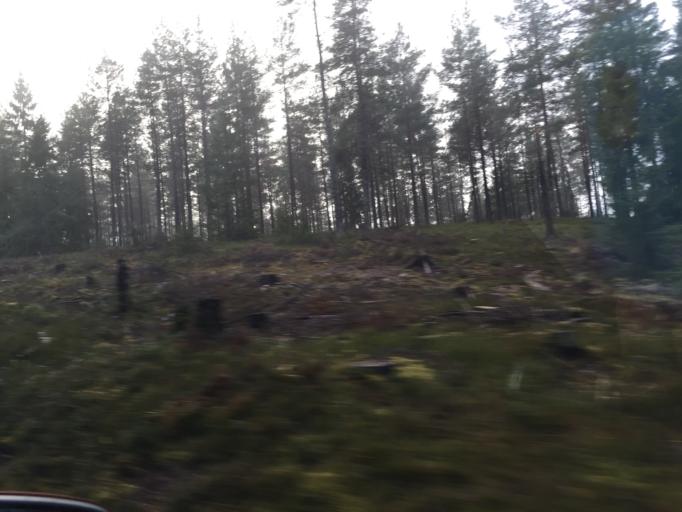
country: SE
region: Stockholm
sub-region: Nynashamns Kommun
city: Osmo
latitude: 59.0901
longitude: 17.8917
